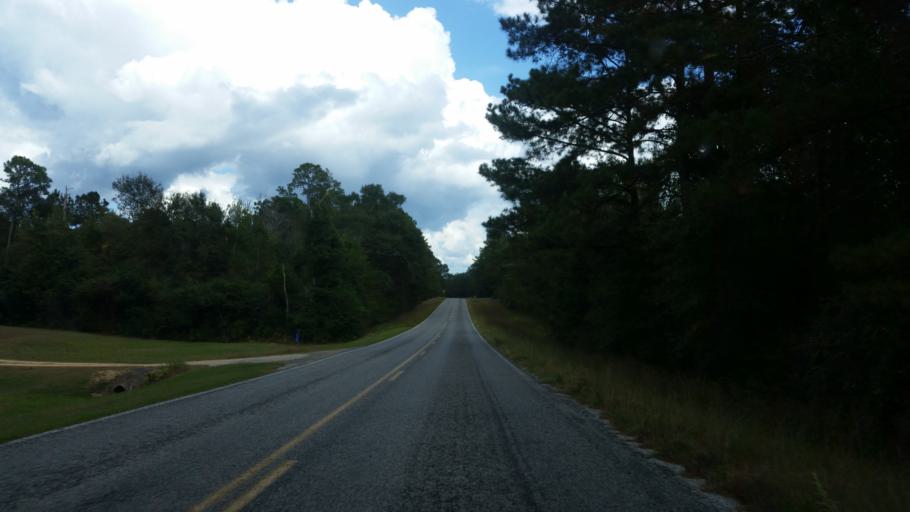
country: US
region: Mississippi
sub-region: Stone County
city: Wiggins
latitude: 30.9298
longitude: -89.0630
